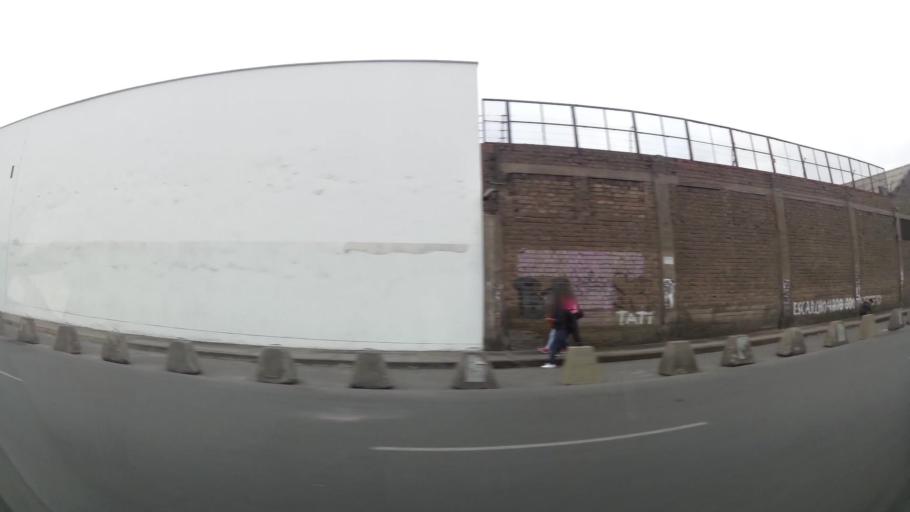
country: PE
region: Lima
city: Lima
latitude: -12.0487
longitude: -77.0577
